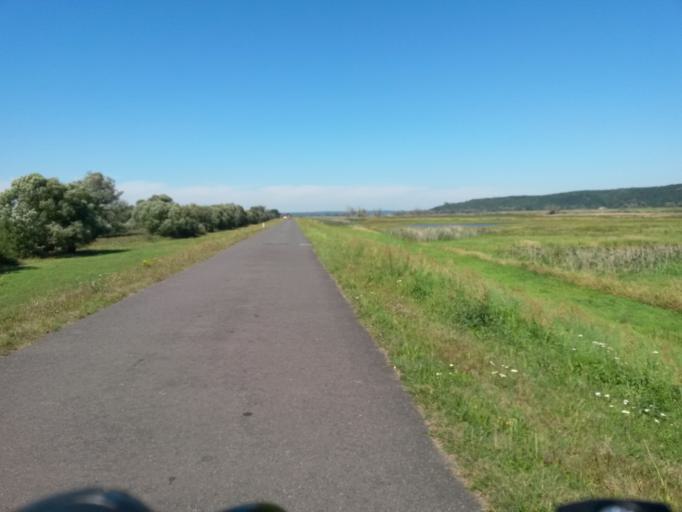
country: PL
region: West Pomeranian Voivodeship
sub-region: Powiat gryfinski
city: Cedynia
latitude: 52.9120
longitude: 14.1452
